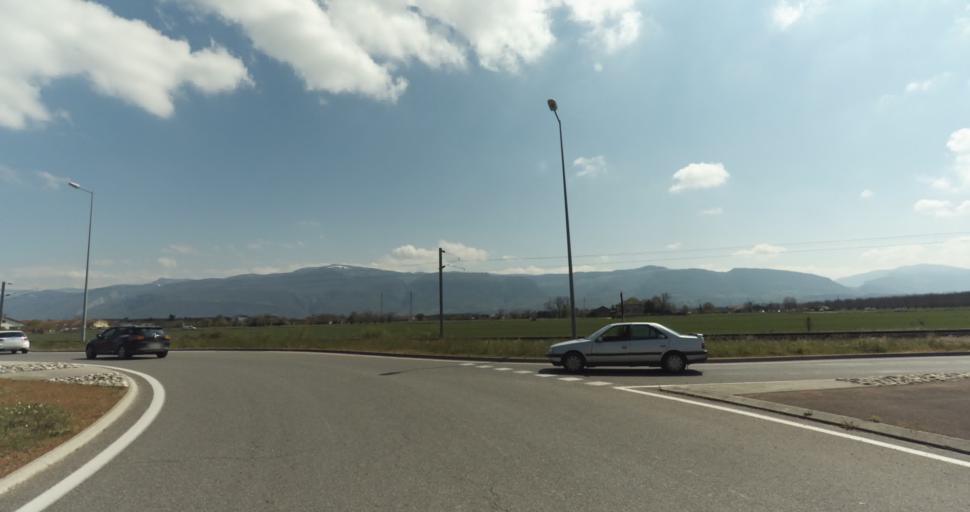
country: FR
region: Rhone-Alpes
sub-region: Departement de l'Isere
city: Saint-Marcellin
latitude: 45.1431
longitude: 5.3058
